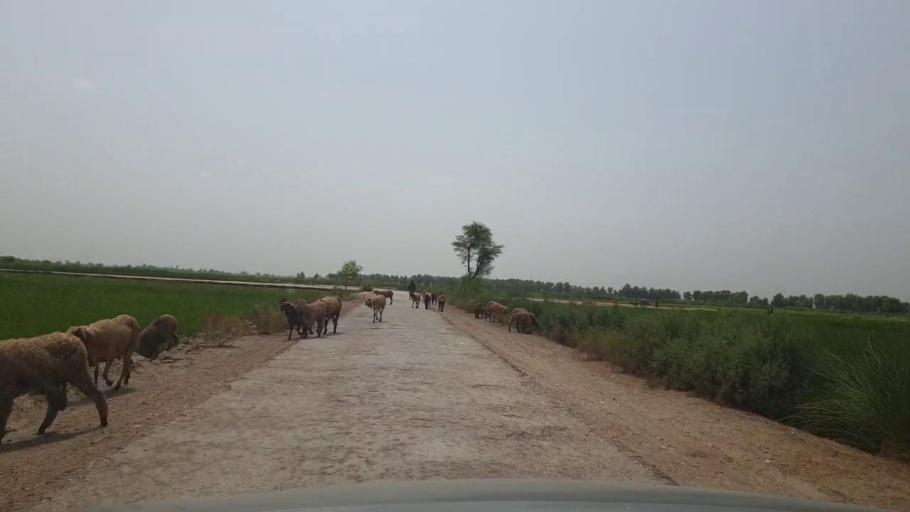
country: PK
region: Sindh
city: Garhi Yasin
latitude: 27.9413
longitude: 68.3802
